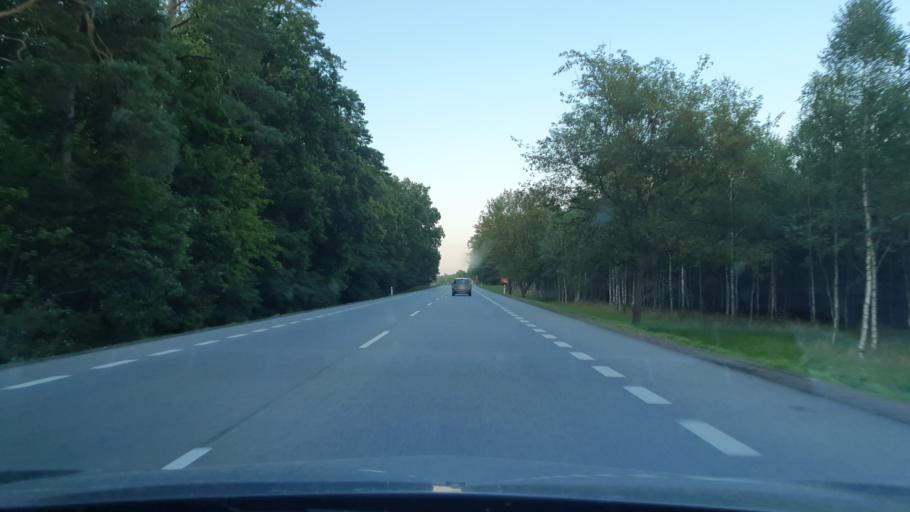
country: PL
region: Pomeranian Voivodeship
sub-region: Powiat leborski
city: Nowa Wies Leborska
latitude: 54.4968
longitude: 17.6188
